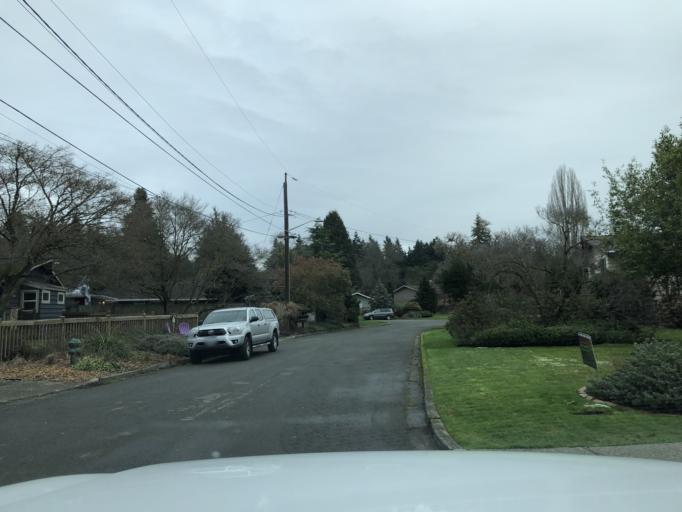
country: US
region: Washington
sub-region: King County
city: Lake Forest Park
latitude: 47.7033
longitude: -122.2837
